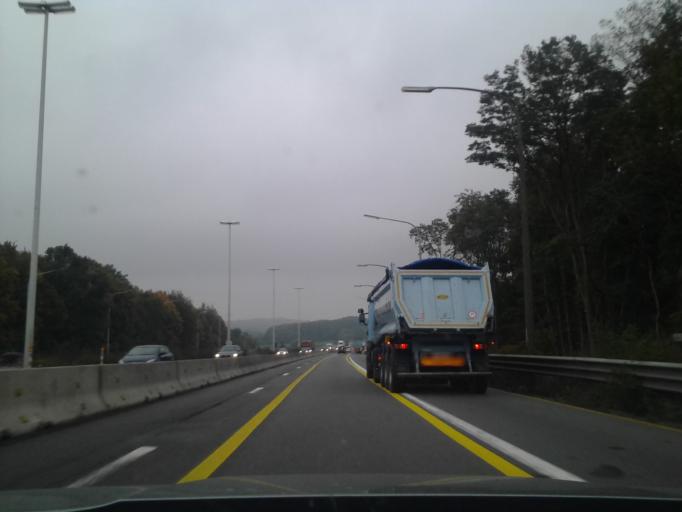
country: BE
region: Wallonia
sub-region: Province du Brabant Wallon
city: Braine-le-Chateau
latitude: 50.6881
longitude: 4.3019
